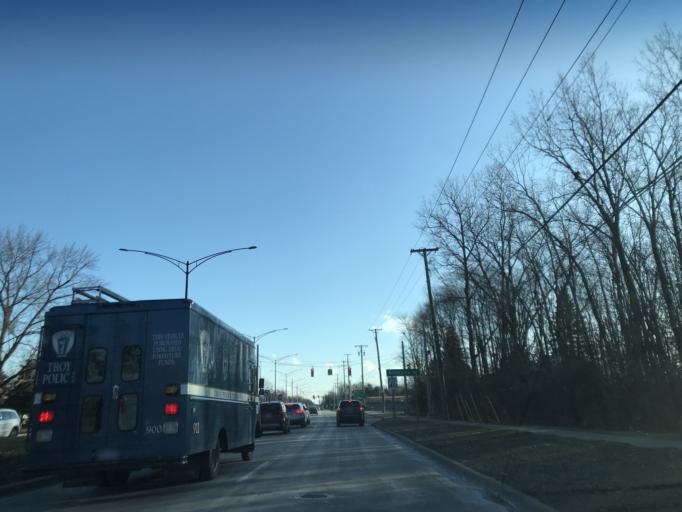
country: US
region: Michigan
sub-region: Oakland County
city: Troy
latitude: 42.5776
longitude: -83.1317
